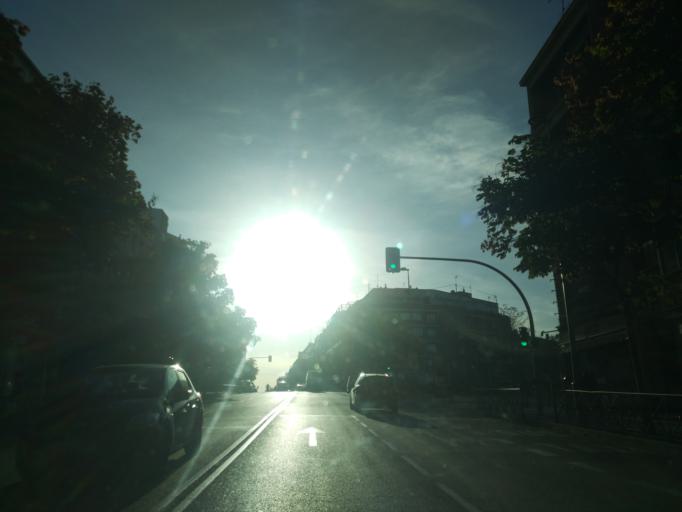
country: ES
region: Madrid
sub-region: Provincia de Madrid
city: Carabanchel
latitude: 40.3920
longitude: -3.7264
